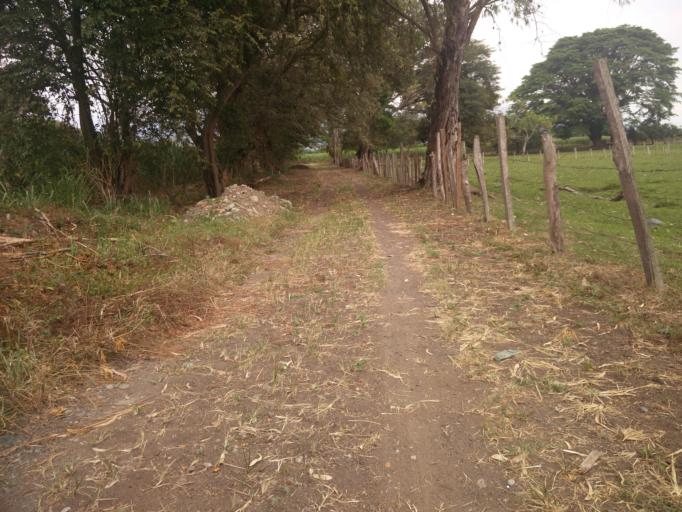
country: CO
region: Valle del Cauca
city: Buga
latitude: 3.8906
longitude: -76.3251
